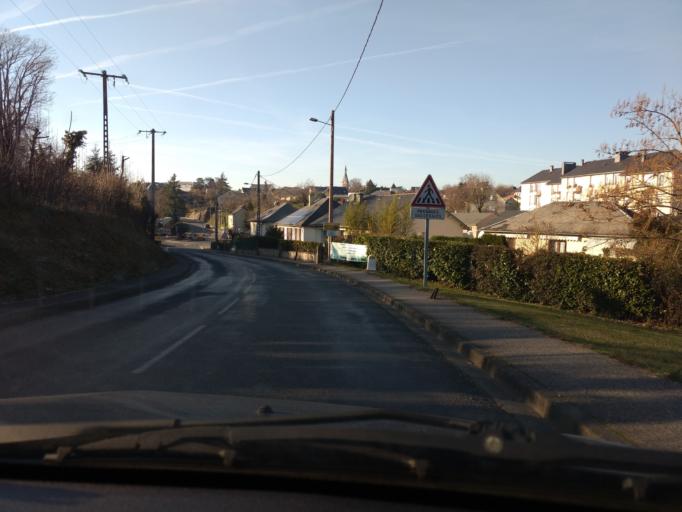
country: FR
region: Midi-Pyrenees
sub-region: Departement de l'Aveyron
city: Naucelle
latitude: 44.1957
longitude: 2.3481
